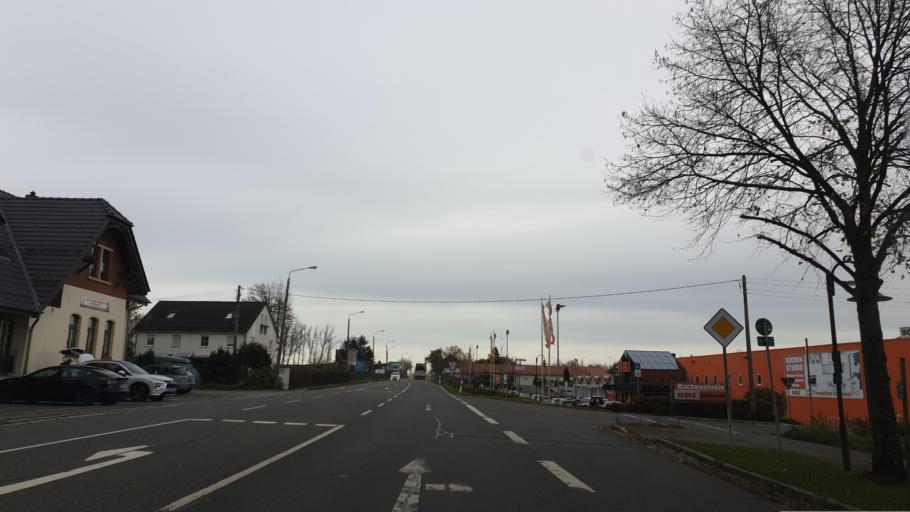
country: DE
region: Saxony
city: Reichenbach/Vogtland
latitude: 50.6375
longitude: 12.3257
